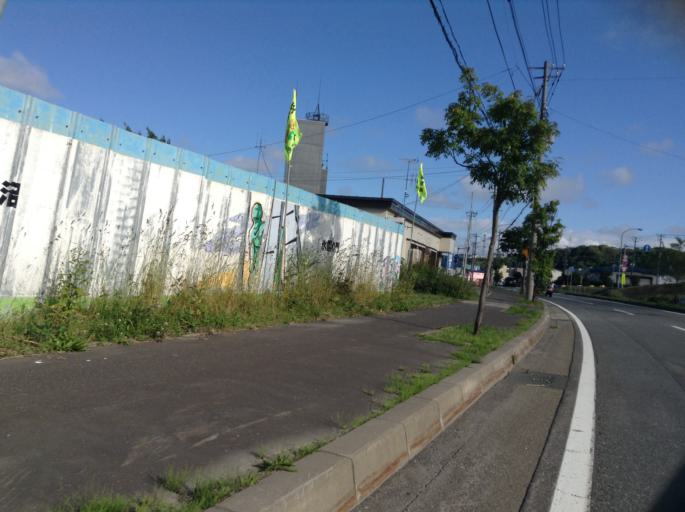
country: JP
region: Hokkaido
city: Wakkanai
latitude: 45.4051
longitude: 141.6760
